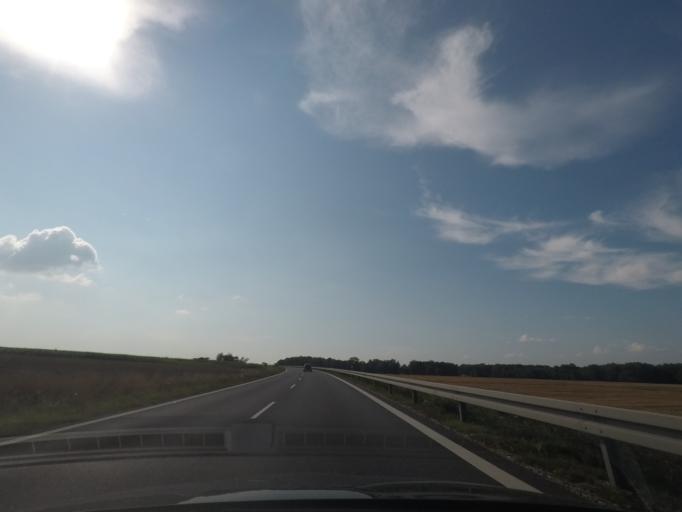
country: PL
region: Silesian Voivodeship
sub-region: Powiat pszczynski
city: Piasek
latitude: 50.0008
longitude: 18.9340
